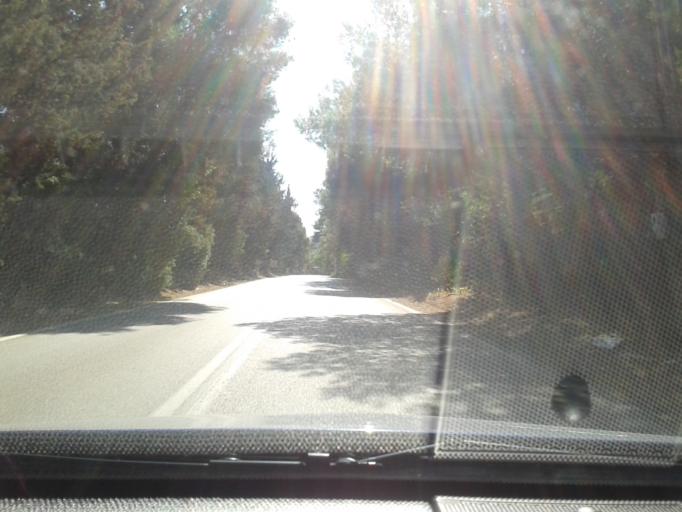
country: GR
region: Attica
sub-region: Nomarchia Athinas
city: Nea Erythraia
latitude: 38.1082
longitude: 23.8048
